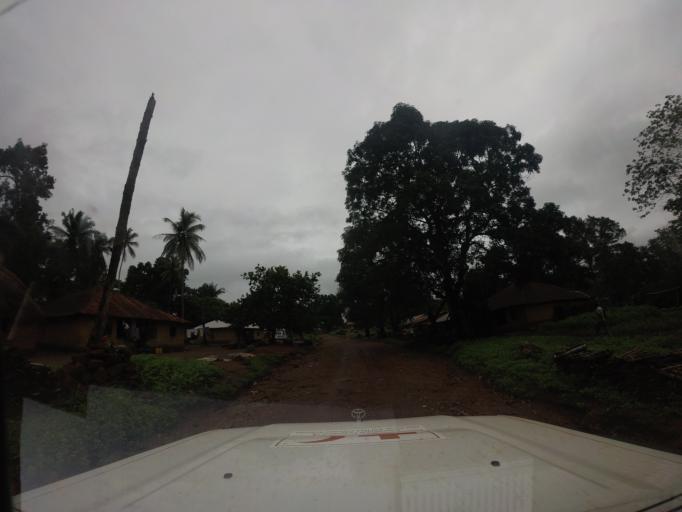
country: SL
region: Northern Province
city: Kambia
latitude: 9.1637
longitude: -12.8782
